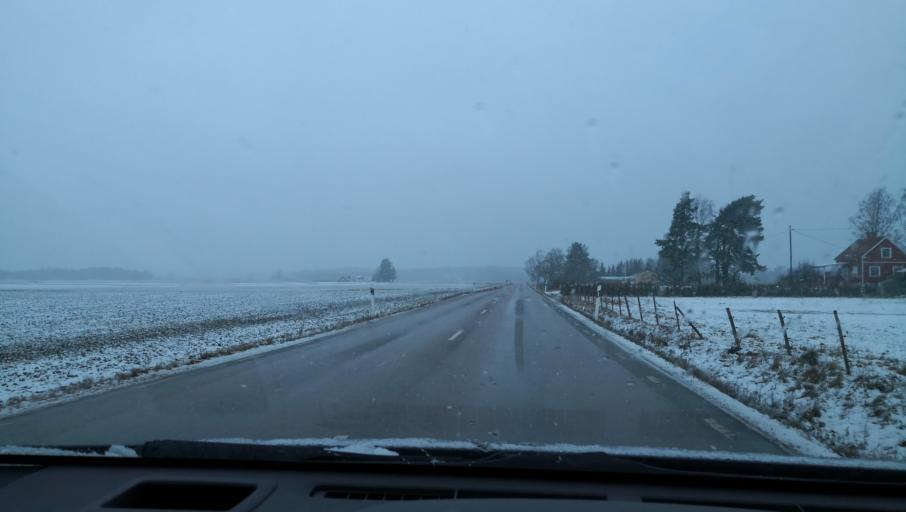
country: SE
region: Vaestmanland
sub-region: Hallstahammars Kommun
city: Kolback
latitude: 59.5989
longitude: 16.2801
